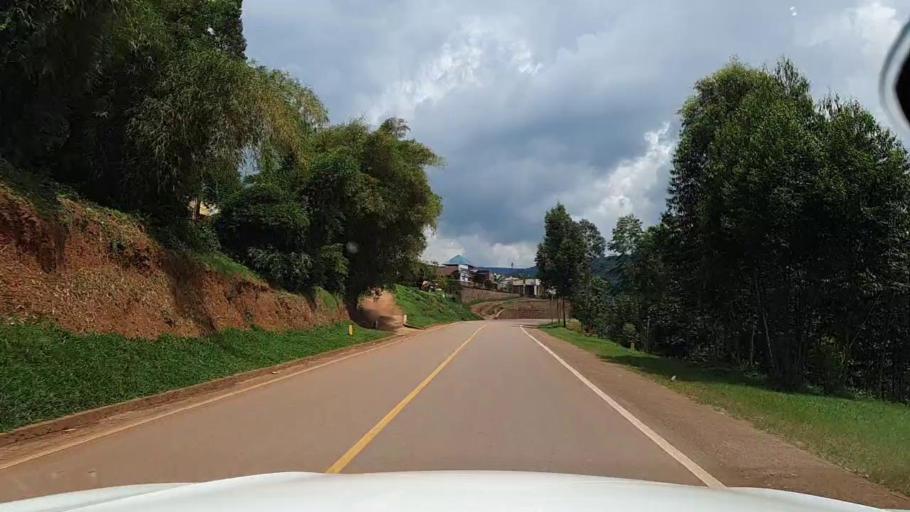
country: RW
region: Kigali
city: Kigali
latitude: -1.8091
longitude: 30.1243
